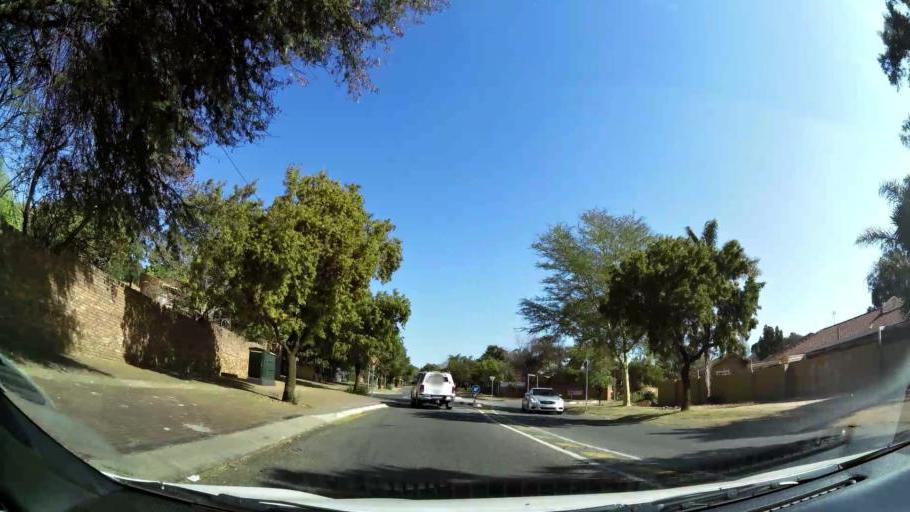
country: ZA
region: Gauteng
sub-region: City of Tshwane Metropolitan Municipality
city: Pretoria
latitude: -25.7908
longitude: 28.2730
